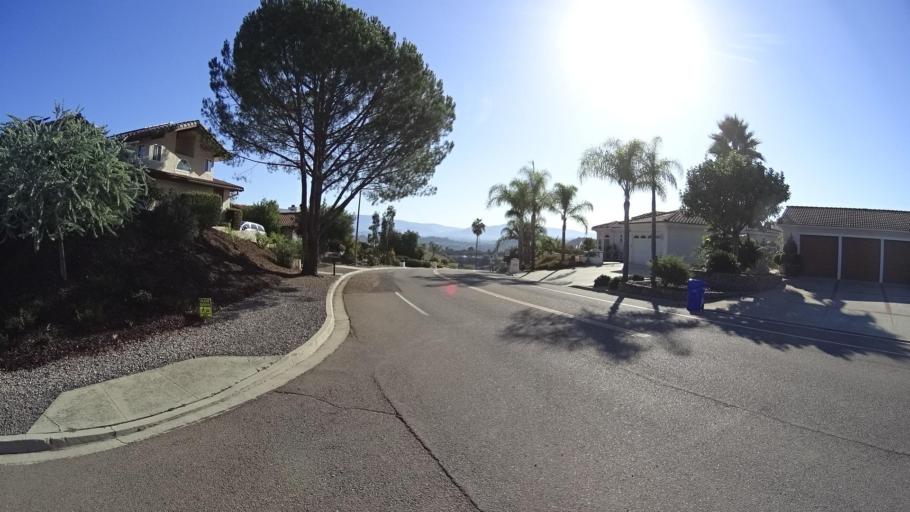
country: US
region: California
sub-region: San Diego County
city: Hidden Meadows
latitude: 33.2213
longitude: -117.1015
